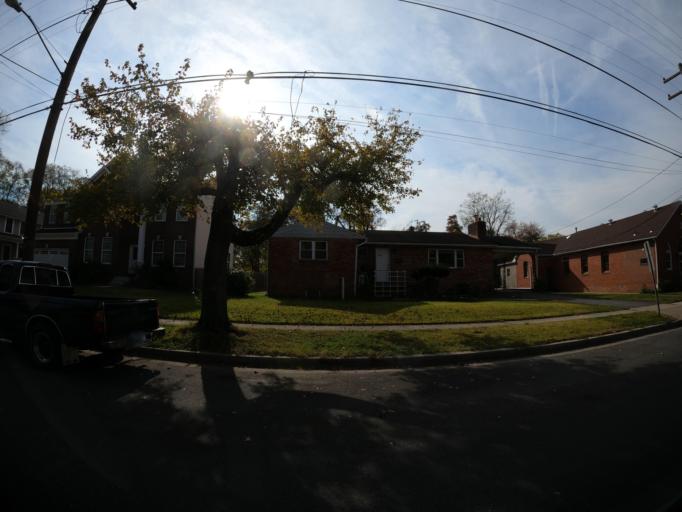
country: US
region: Maryland
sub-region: Prince George's County
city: College Park
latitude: 38.9886
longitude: -76.9257
